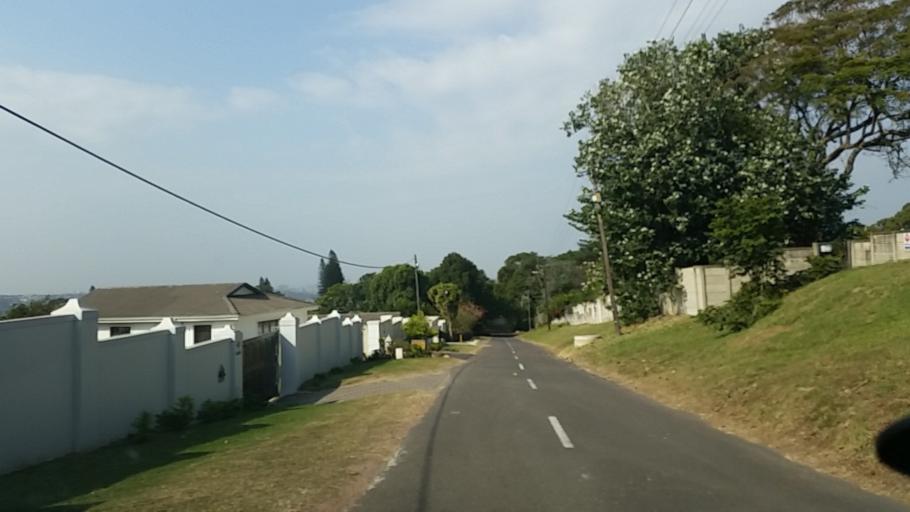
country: ZA
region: KwaZulu-Natal
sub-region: eThekwini Metropolitan Municipality
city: Berea
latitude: -29.8385
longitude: 30.9381
